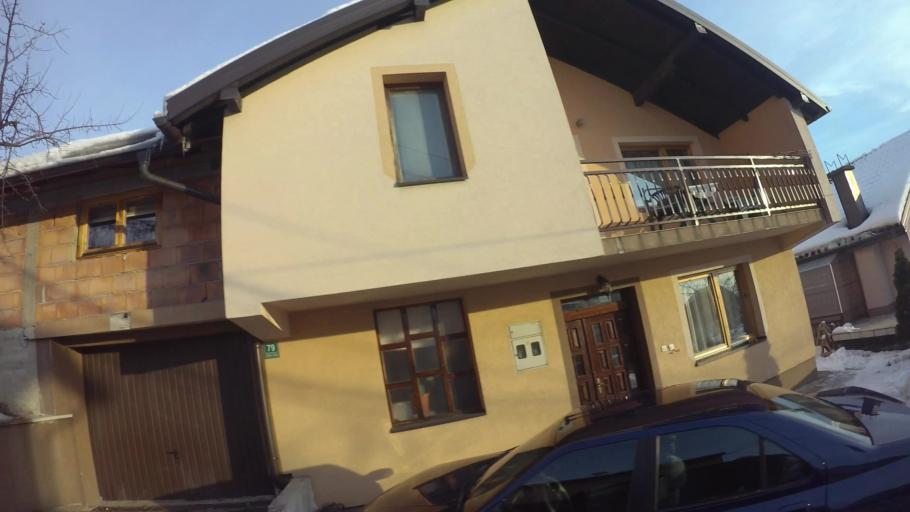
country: BA
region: Federation of Bosnia and Herzegovina
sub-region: Kanton Sarajevo
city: Sarajevo
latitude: 43.8369
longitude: 18.3607
